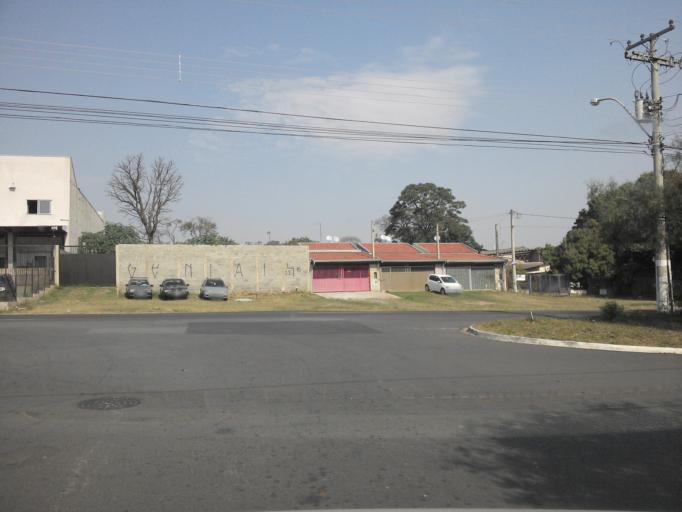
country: BR
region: Sao Paulo
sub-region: Hortolandia
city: Hortolandia
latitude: -22.8868
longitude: -47.1645
